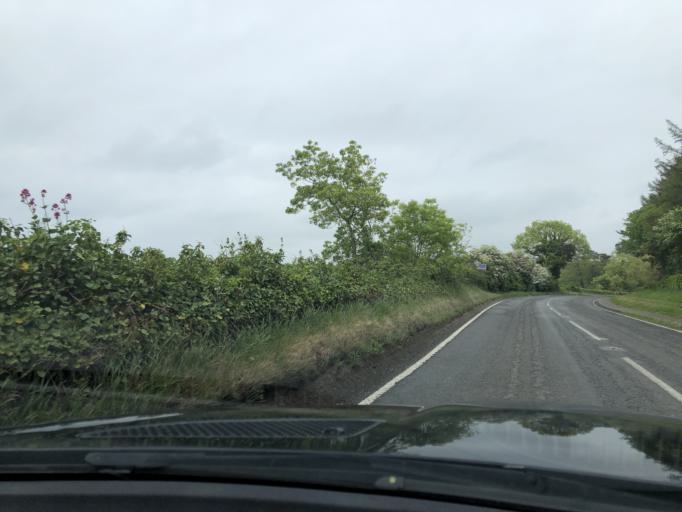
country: GB
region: Northern Ireland
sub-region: Down District
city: Portaferry
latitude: 54.3651
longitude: -5.5641
